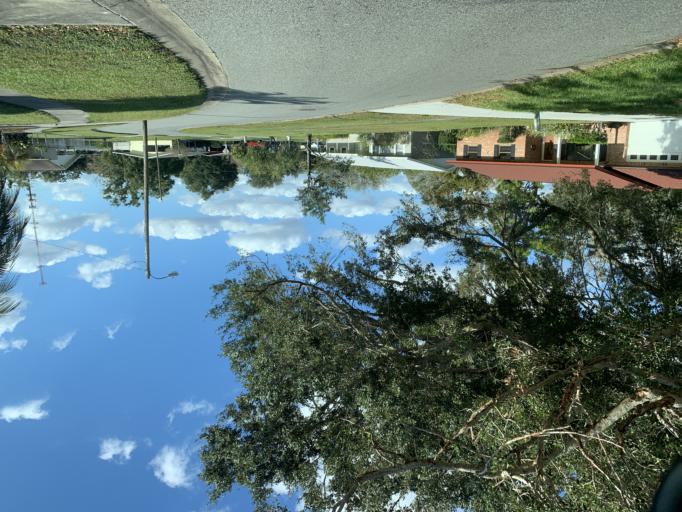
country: US
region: Florida
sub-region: Orange County
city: Eatonville
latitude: 28.6114
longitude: -81.3965
